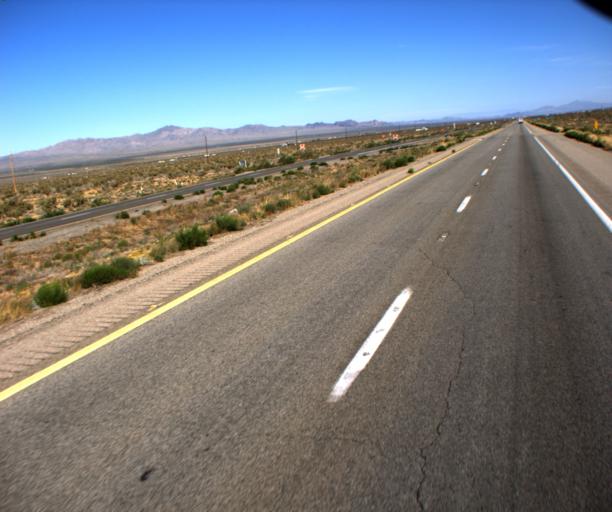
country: US
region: Arizona
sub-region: Mohave County
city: Dolan Springs
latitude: 35.4871
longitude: -114.3227
